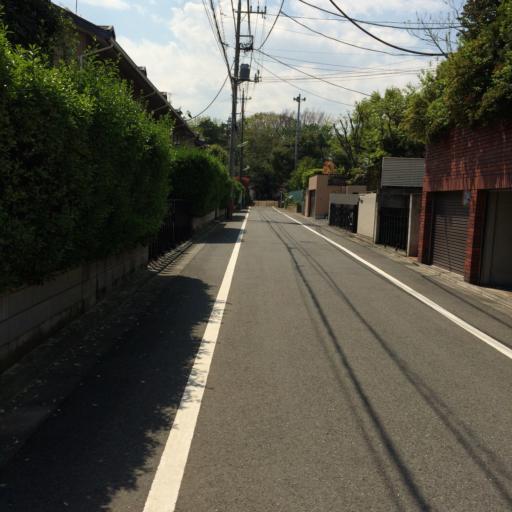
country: JP
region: Tokyo
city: Tokyo
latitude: 35.6580
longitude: 139.6581
